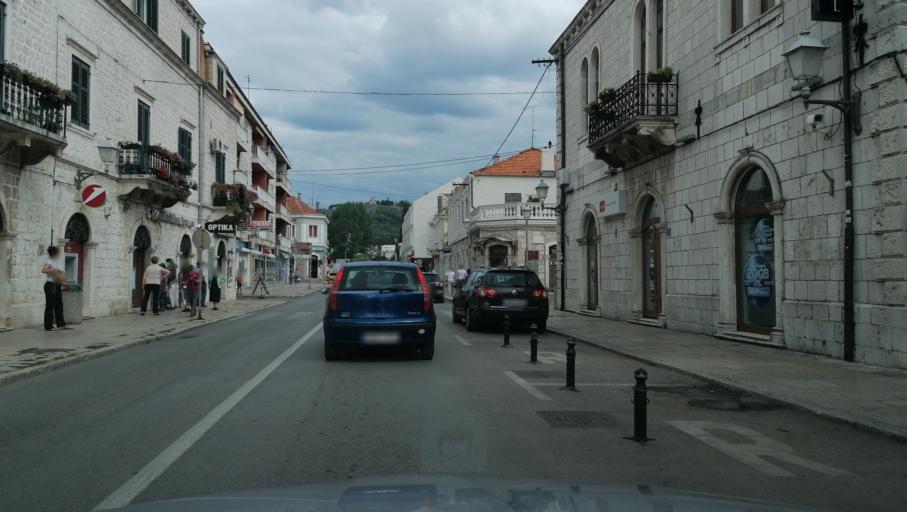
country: BA
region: Republika Srpska
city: Trebinje
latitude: 42.7120
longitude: 18.3450
